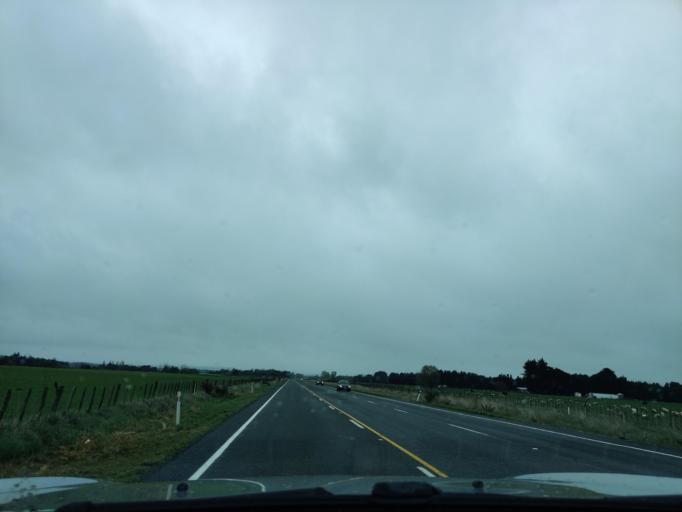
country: NZ
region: Hawke's Bay
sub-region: Hastings District
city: Hastings
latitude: -40.0205
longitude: 176.3050
